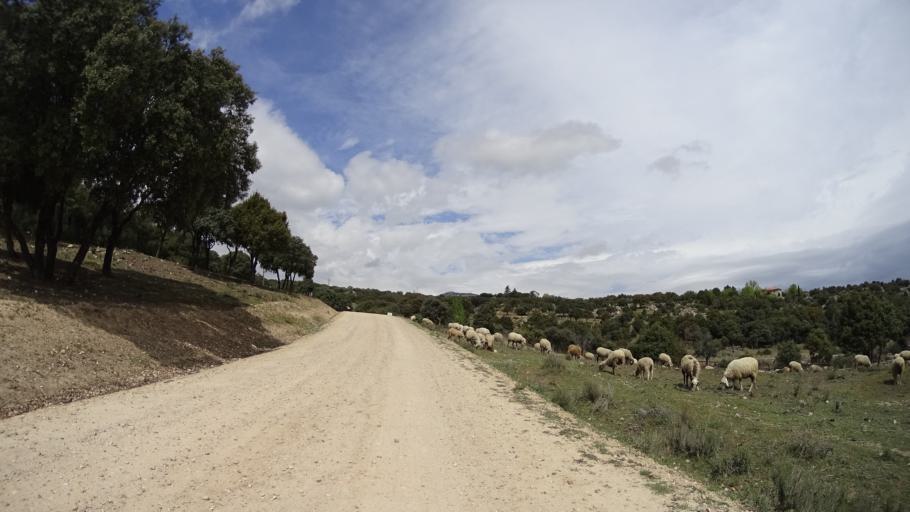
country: ES
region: Madrid
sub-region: Provincia de Madrid
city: Hoyo de Manzanares
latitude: 40.6195
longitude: -3.8824
